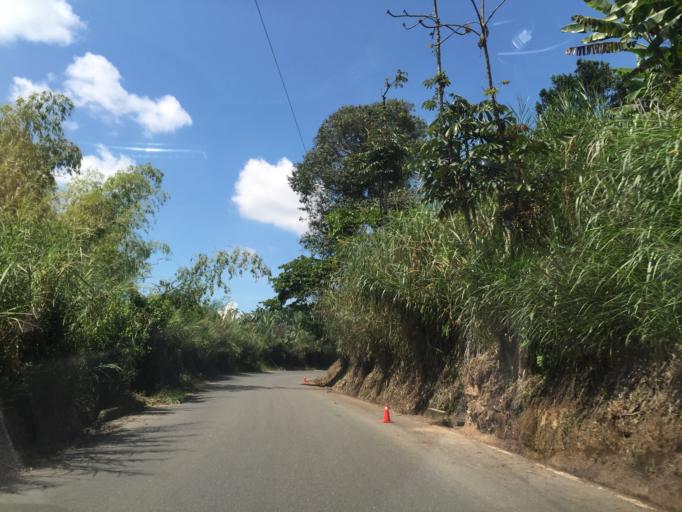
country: CO
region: Valle del Cauca
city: Alcala
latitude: 4.6925
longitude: -75.7847
